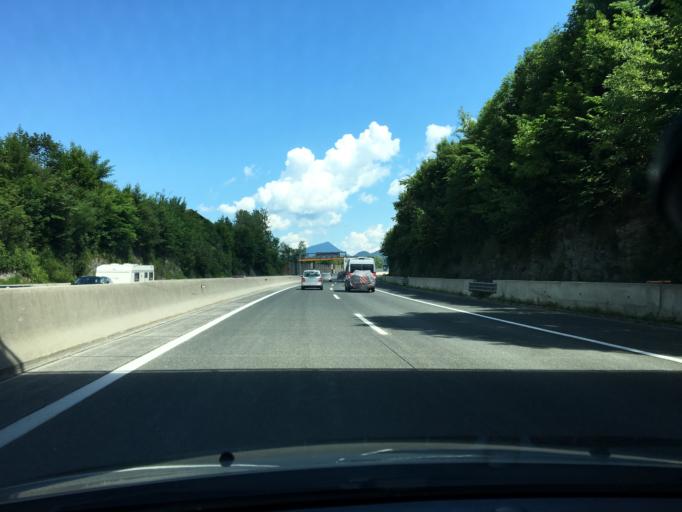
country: AT
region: Salzburg
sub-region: Politischer Bezirk Hallein
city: Kuchl
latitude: 47.6307
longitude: 13.1317
